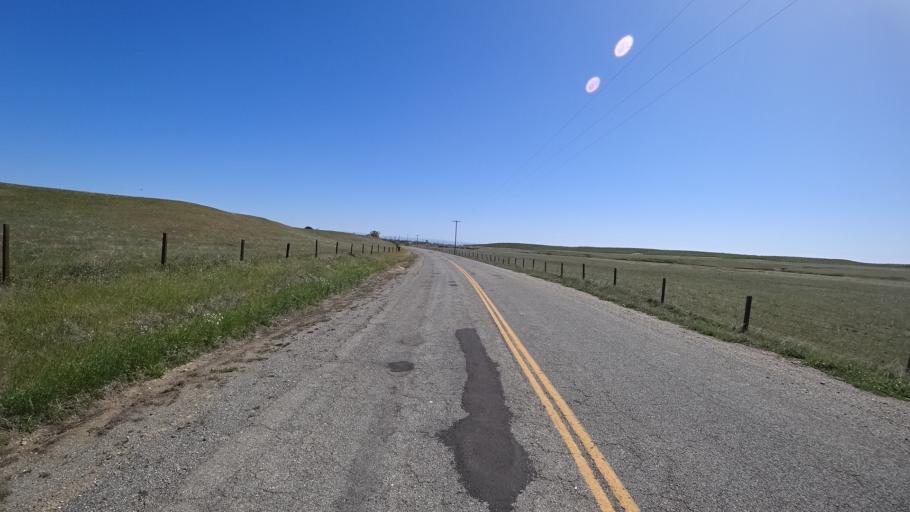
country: US
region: California
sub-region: Glenn County
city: Orland
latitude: 39.7802
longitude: -122.3023
